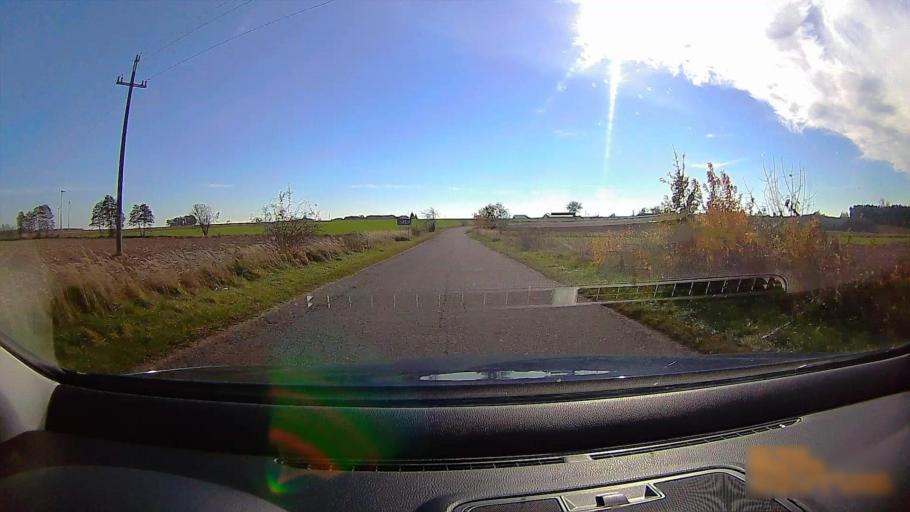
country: PL
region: Greater Poland Voivodeship
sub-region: Powiat ostrzeszowski
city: Doruchow
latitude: 51.4003
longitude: 18.0292
